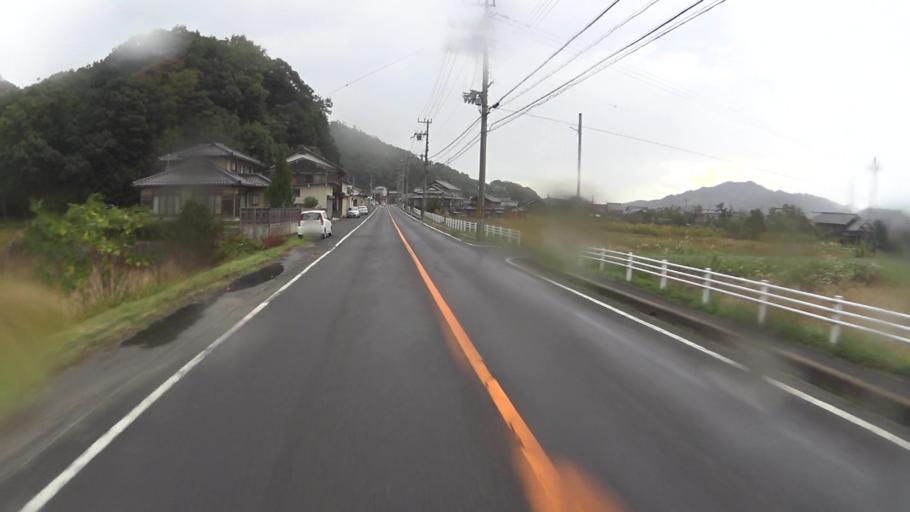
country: JP
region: Kyoto
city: Miyazu
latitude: 35.5532
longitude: 135.2348
